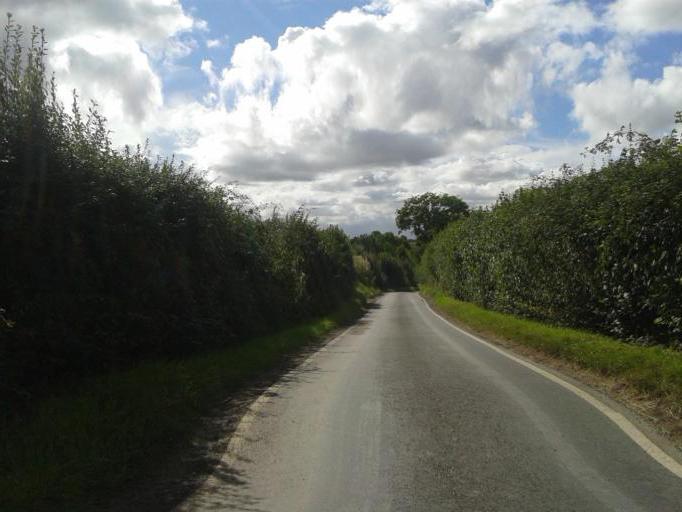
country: GB
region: England
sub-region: Hertfordshire
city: Reed
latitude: 51.9939
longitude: 0.0972
